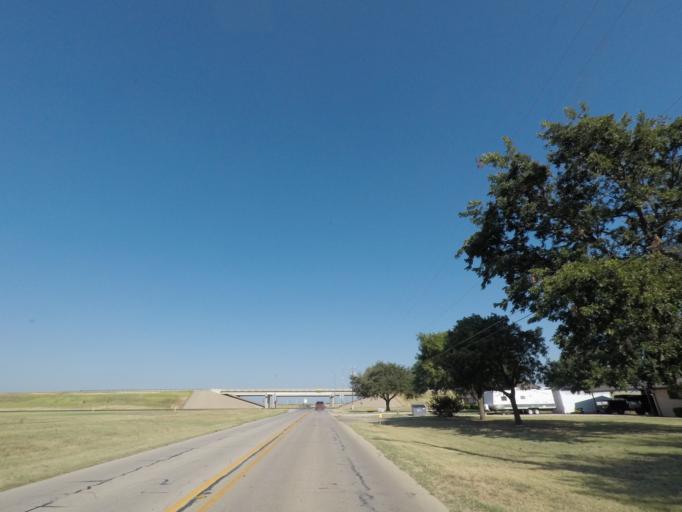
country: US
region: Texas
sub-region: Baylor County
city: Seymour
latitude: 33.5958
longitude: -99.2432
